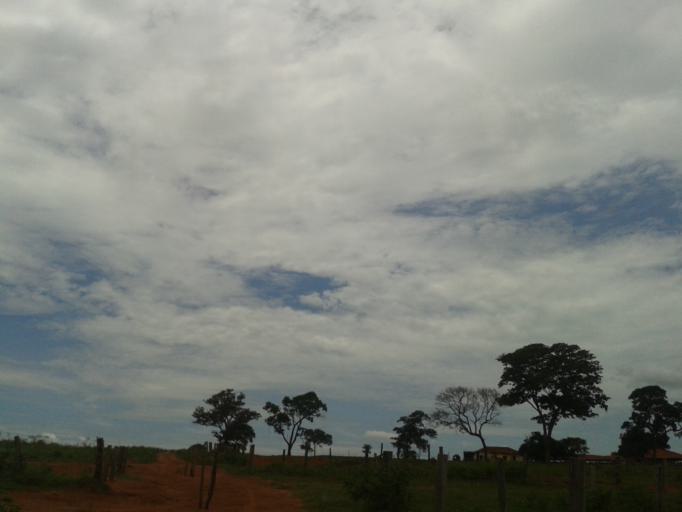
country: BR
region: Minas Gerais
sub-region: Santa Vitoria
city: Santa Vitoria
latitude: -19.2183
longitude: -50.5985
